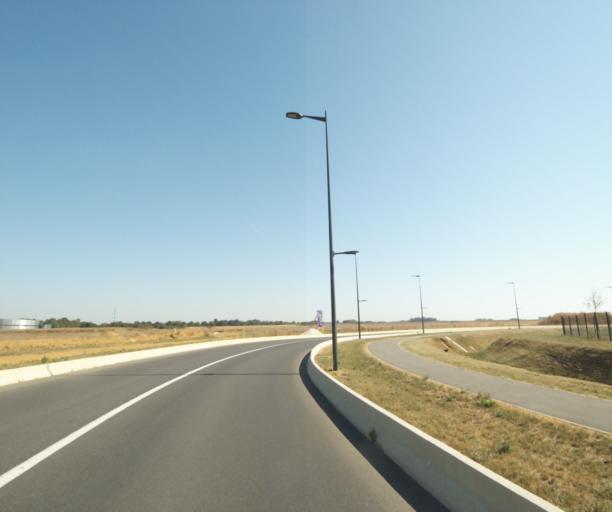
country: FR
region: Ile-de-France
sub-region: Departement de Seine-et-Marne
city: Moissy-Cramayel
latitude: 48.6132
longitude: 2.5956
